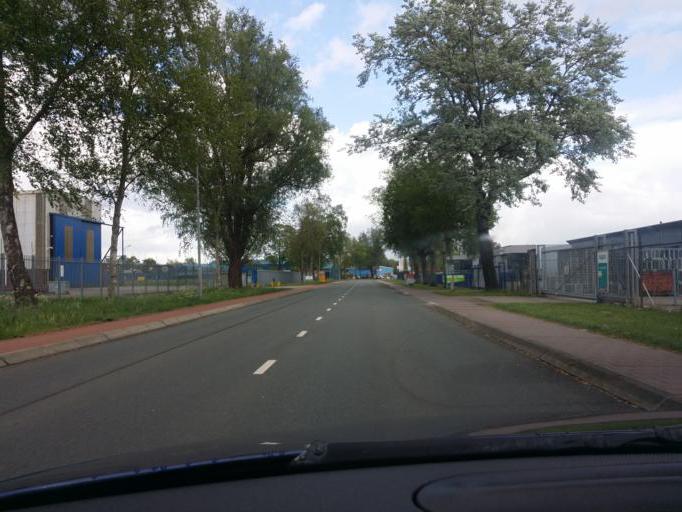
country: NL
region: Groningen
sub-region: Gemeente Hoogezand-Sappemeer
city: Hoogezand
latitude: 53.1662
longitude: 6.7344
